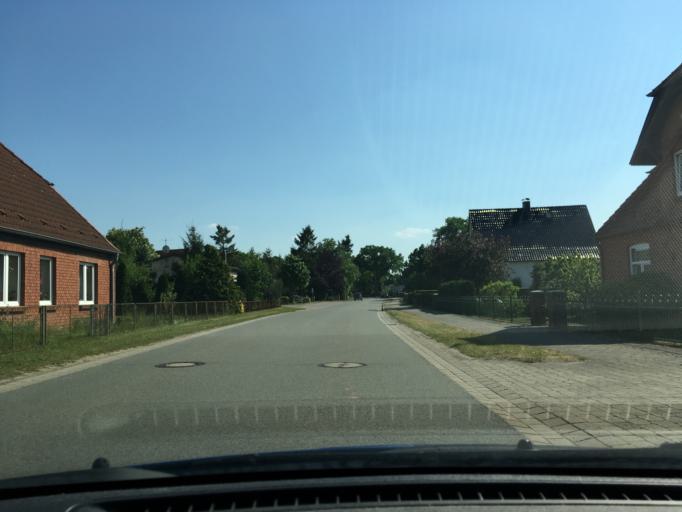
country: DE
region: Lower Saxony
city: Hitzacker
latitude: 53.1979
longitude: 11.0427
